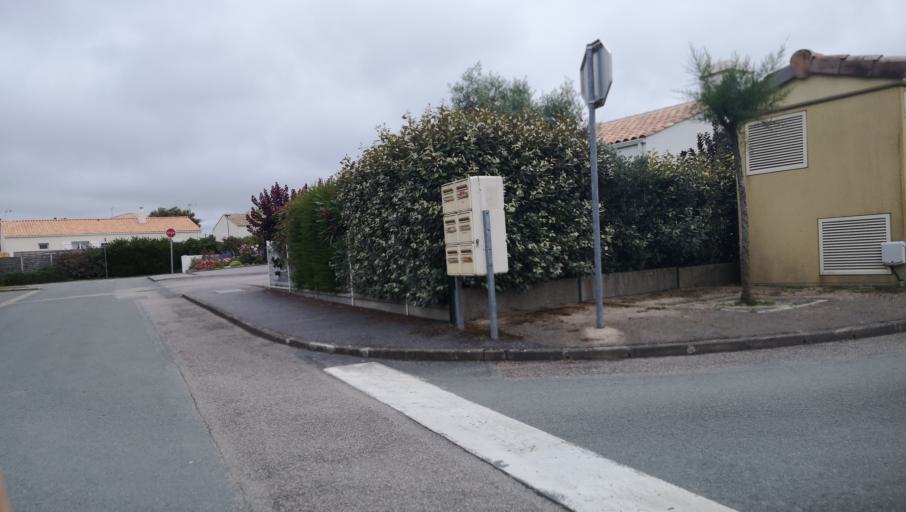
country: FR
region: Pays de la Loire
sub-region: Departement de la Vendee
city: Les Sables-d'Olonne
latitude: 46.5091
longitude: -1.7836
